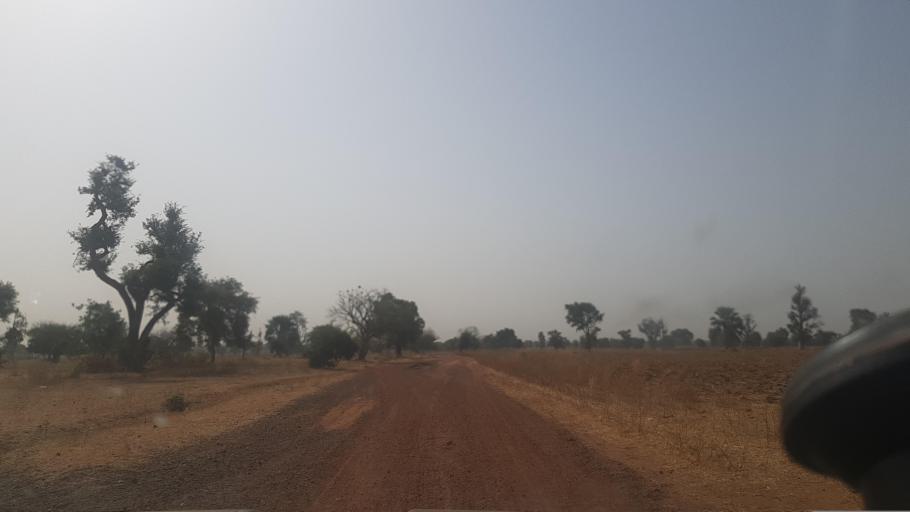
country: ML
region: Segou
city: Baroueli
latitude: 13.1501
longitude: -6.5162
